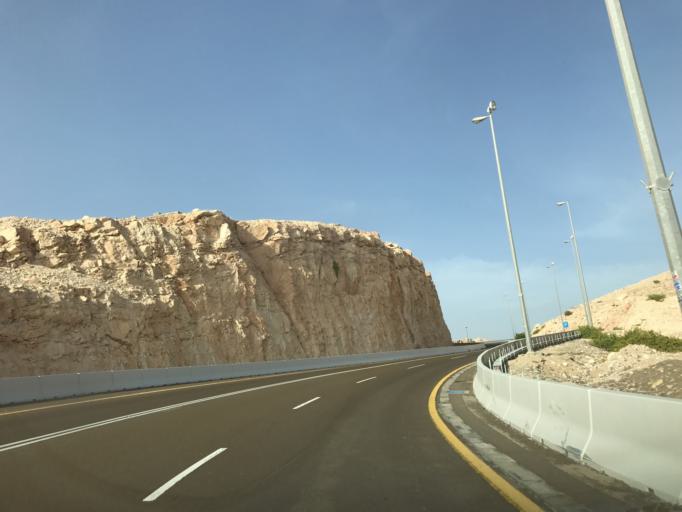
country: AE
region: Abu Dhabi
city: Al Ain
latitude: 24.0832
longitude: 55.7632
